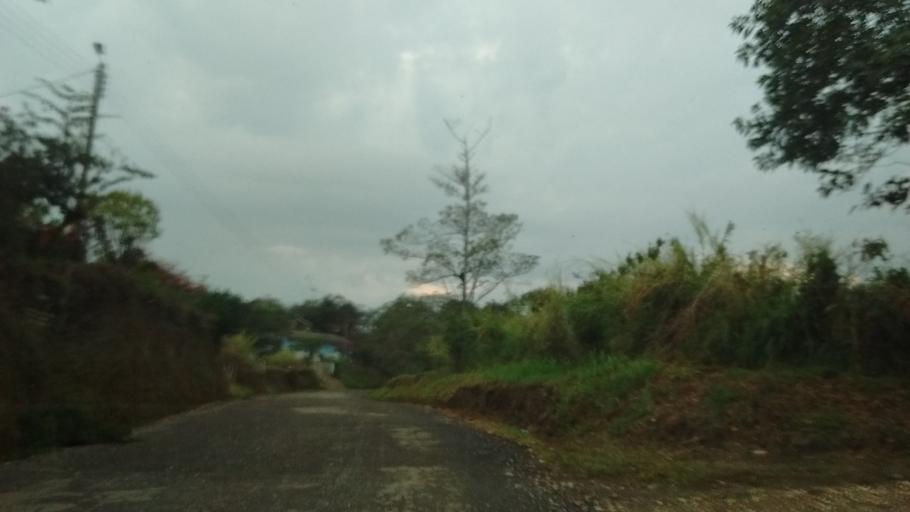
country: CO
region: Cauca
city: Lopez
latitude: 2.3959
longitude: -76.7455
